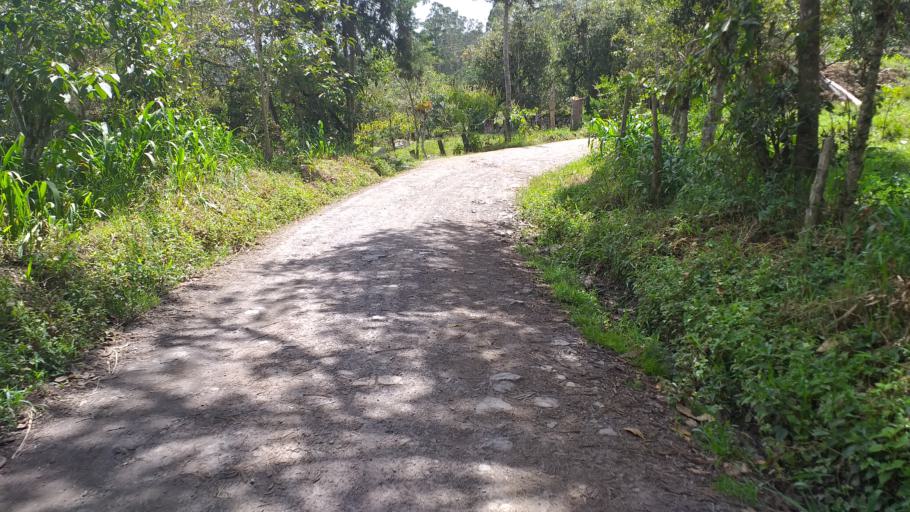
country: CO
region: Cundinamarca
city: Tenza
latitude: 5.1098
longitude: -73.4551
